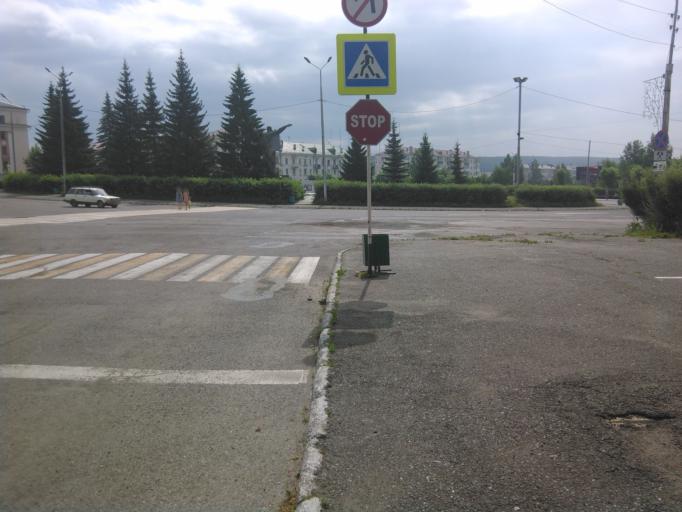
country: RU
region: Sverdlovsk
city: Krasnotur'insk
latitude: 59.7646
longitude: 60.1925
